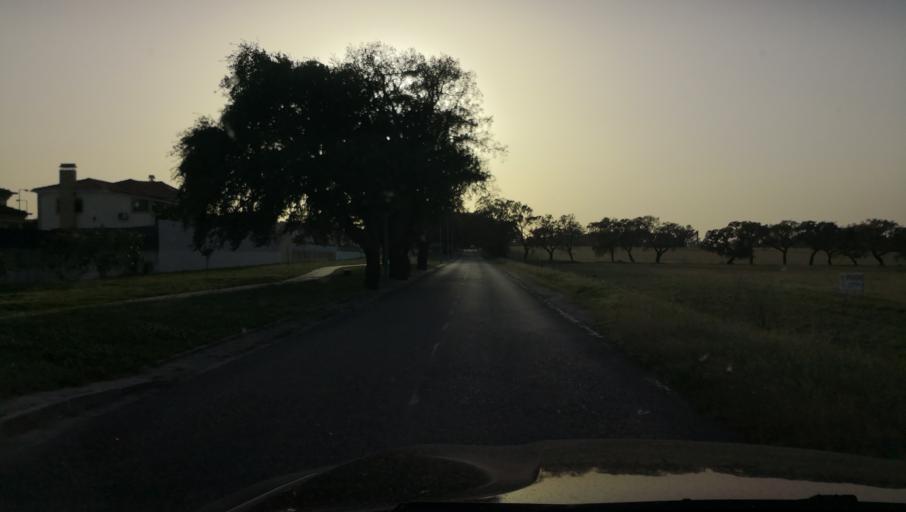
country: PT
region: Setubal
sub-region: Setubal
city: Setubal
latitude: 38.5368
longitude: -8.8236
